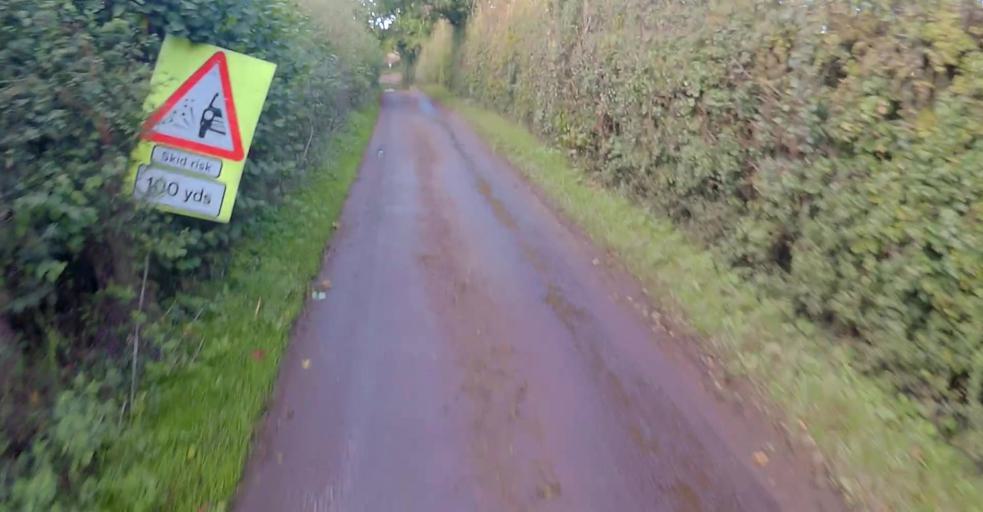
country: GB
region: England
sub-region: Surrey
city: Farnham
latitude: 51.2070
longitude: -0.8470
